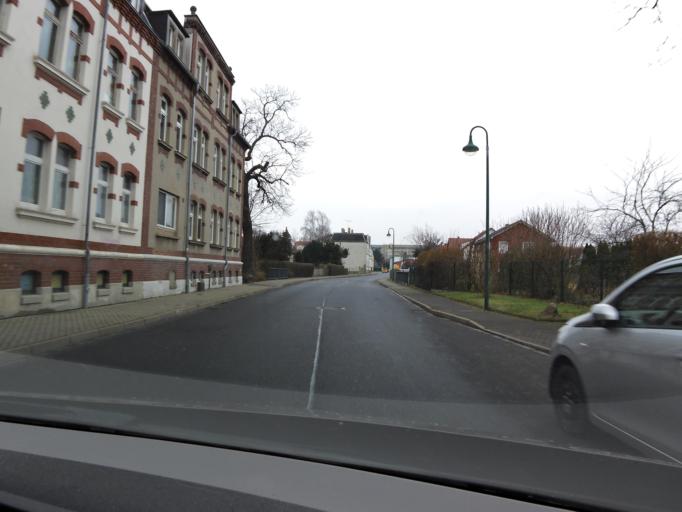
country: DE
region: Saxony
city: Markranstadt
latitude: 51.3204
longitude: 12.2581
